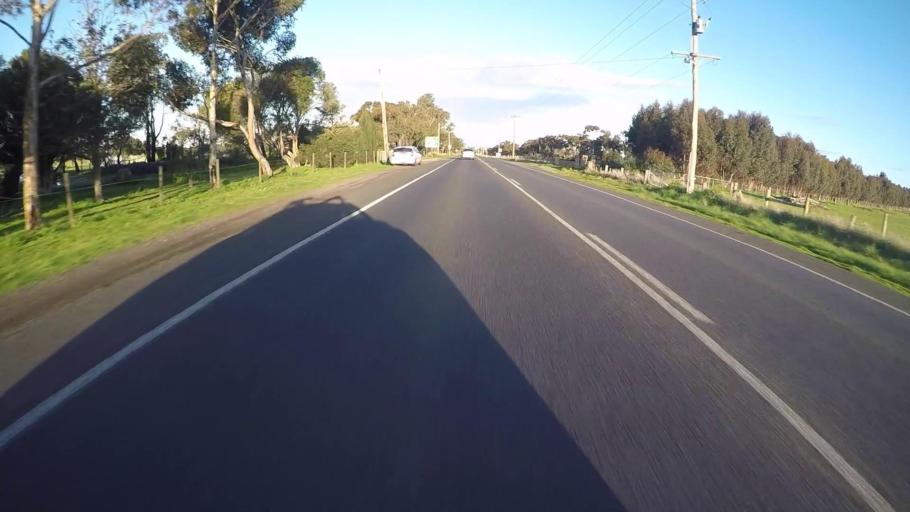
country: AU
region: Victoria
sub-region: Greater Geelong
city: Wandana Heights
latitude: -38.1375
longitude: 144.2855
